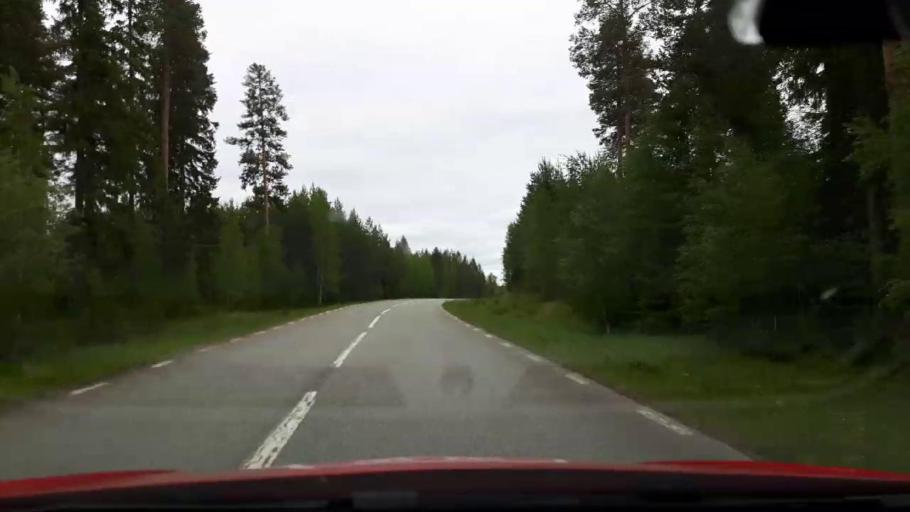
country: SE
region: Jaemtland
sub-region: Stroemsunds Kommun
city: Stroemsund
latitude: 63.3869
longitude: 15.6784
